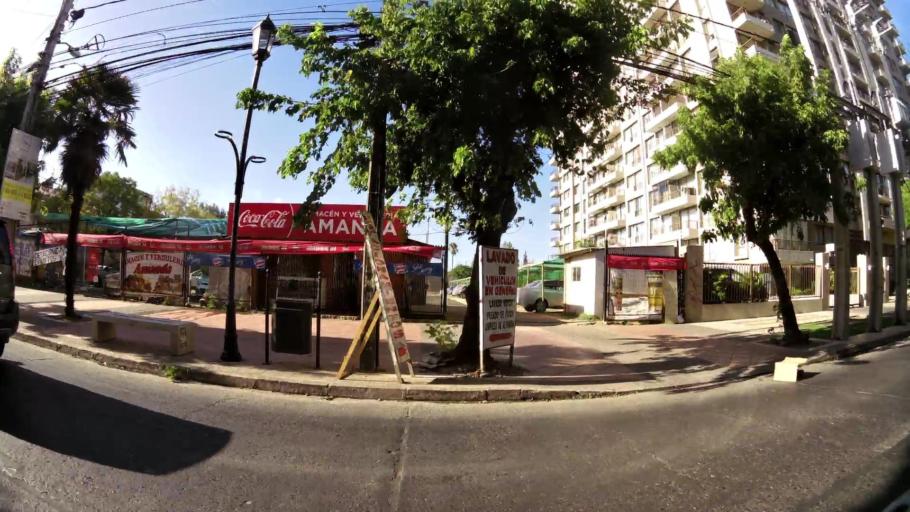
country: CL
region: Maule
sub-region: Provincia de Talca
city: Talca
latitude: -35.4218
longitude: -71.6632
